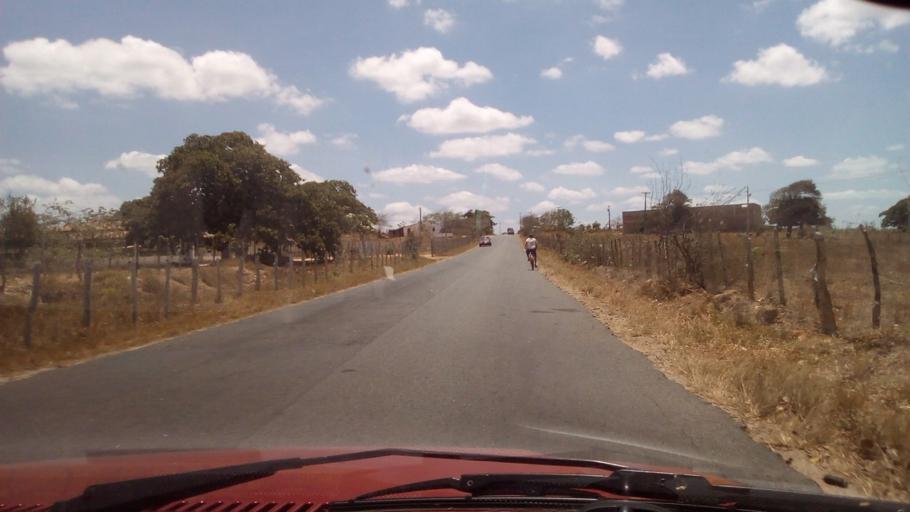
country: BR
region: Paraiba
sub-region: Cacimba De Dentro
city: Cacimba de Dentro
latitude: -6.6193
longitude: -35.7998
